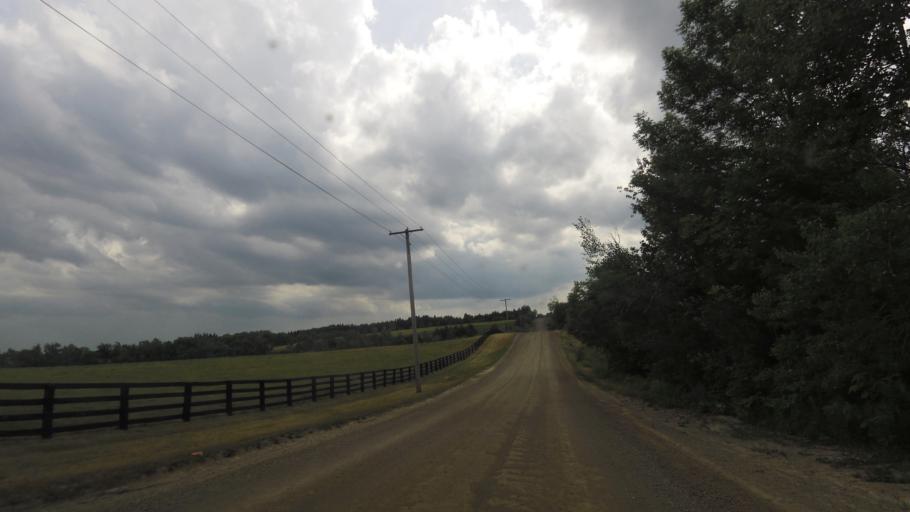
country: CA
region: Ontario
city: Orangeville
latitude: 43.8639
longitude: -79.9430
